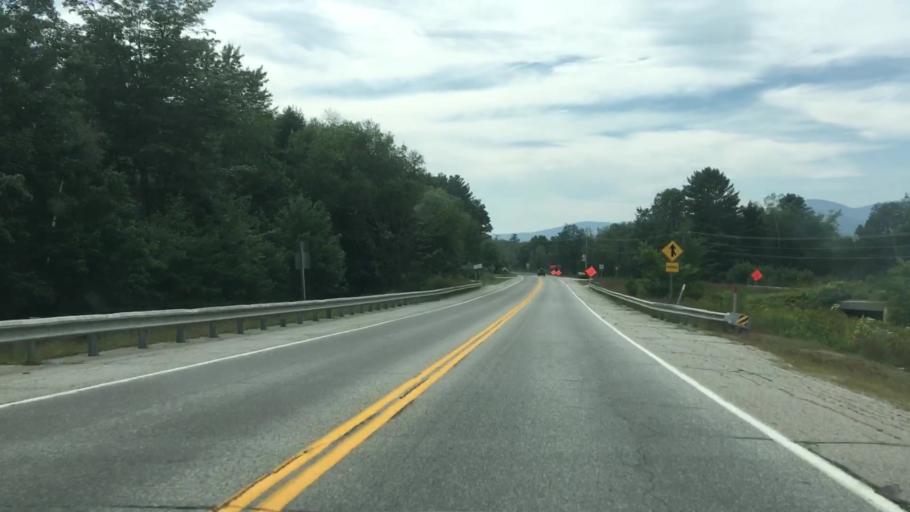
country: US
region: Maine
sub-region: Oxford County
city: Bethel
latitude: 44.4092
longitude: -70.7986
